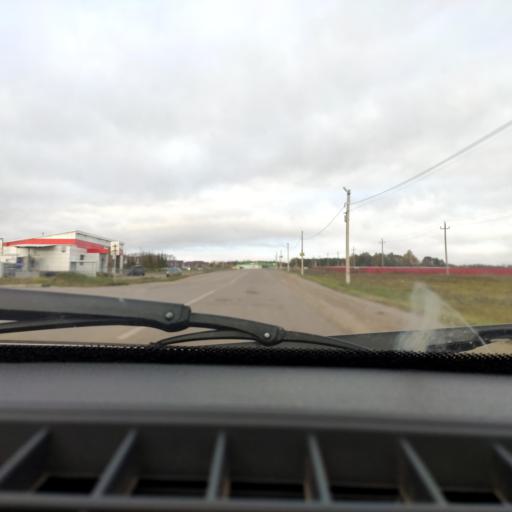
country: RU
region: Bashkortostan
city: Avdon
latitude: 54.6589
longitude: 55.7429
